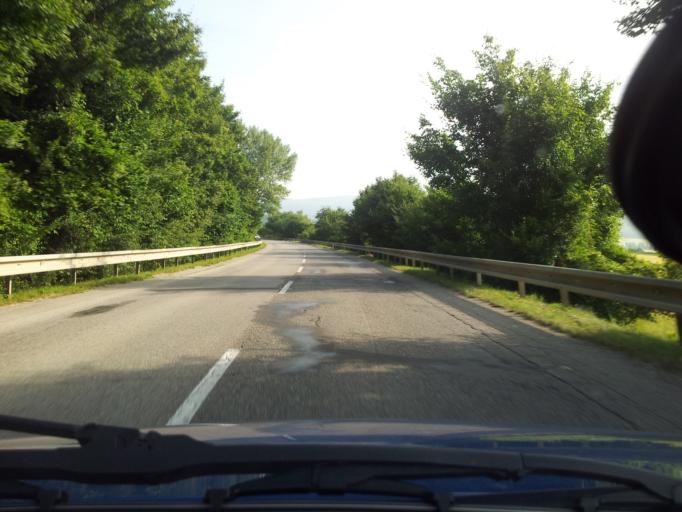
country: SK
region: Nitriansky
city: Partizanske
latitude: 48.6683
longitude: 18.3690
